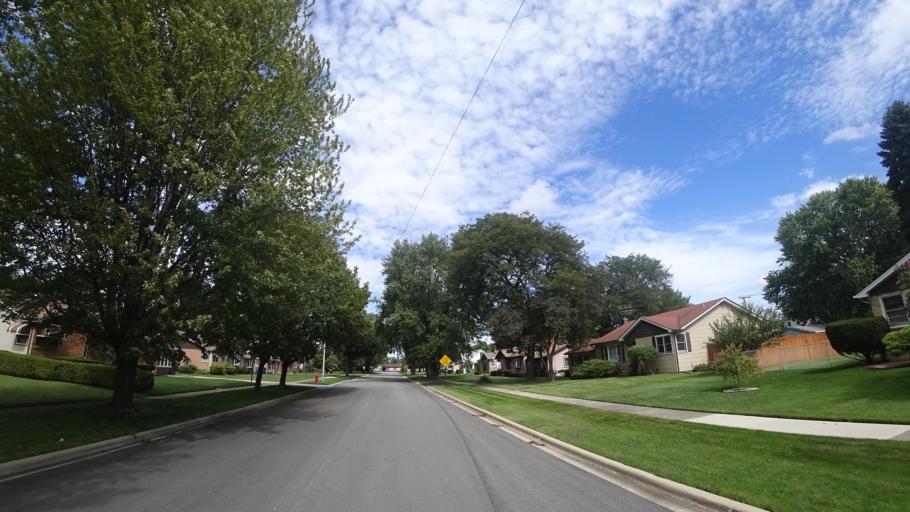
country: US
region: Illinois
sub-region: Cook County
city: Chicago Ridge
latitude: 41.7028
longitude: -87.7858
